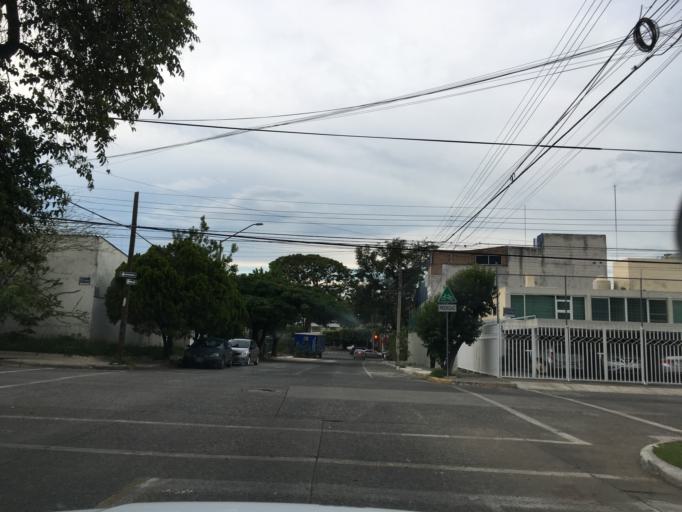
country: MX
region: Jalisco
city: Guadalajara
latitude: 20.6656
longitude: -103.3826
